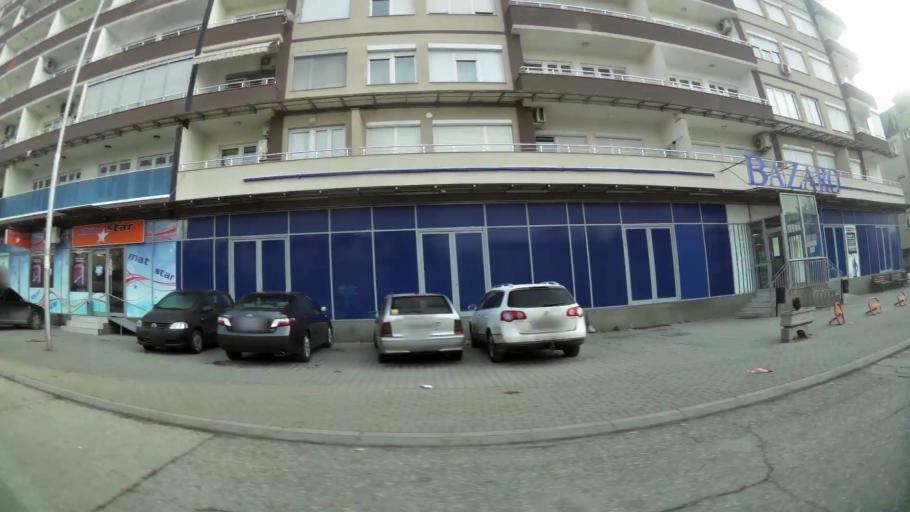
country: MK
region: Cair
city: Cair
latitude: 42.0172
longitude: 21.4360
